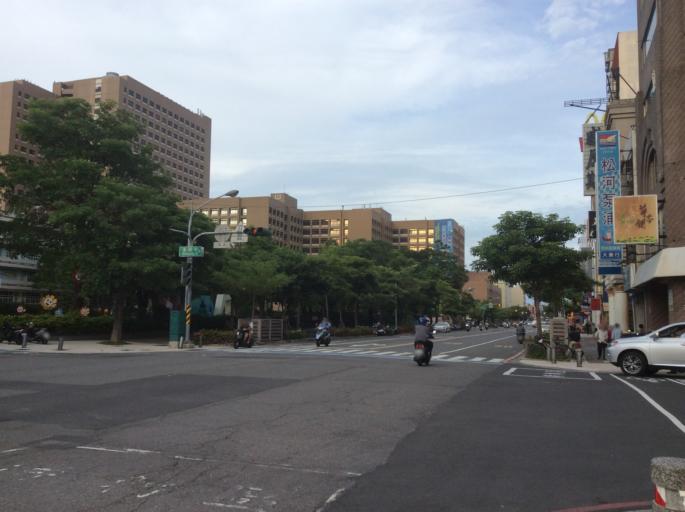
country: TW
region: Kaohsiung
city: Kaohsiung
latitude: 22.6450
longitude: 120.3075
